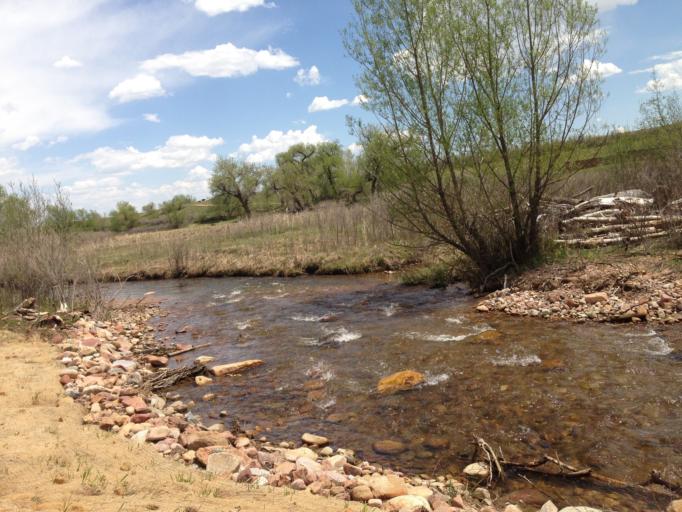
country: US
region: Colorado
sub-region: Boulder County
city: Superior
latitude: 39.9694
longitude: -105.2272
